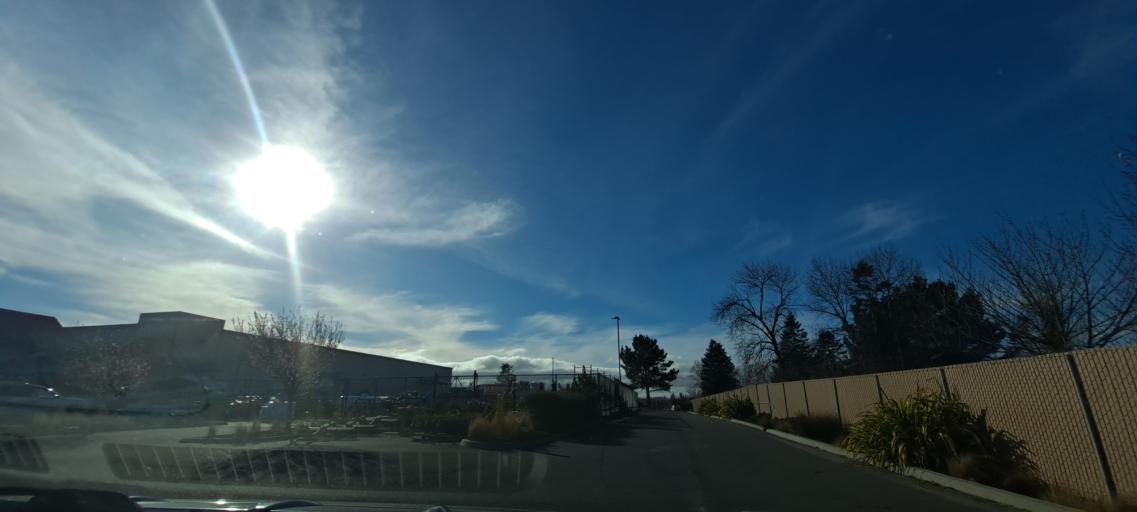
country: US
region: California
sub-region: Humboldt County
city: Fortuna
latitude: 40.5841
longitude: -124.1550
